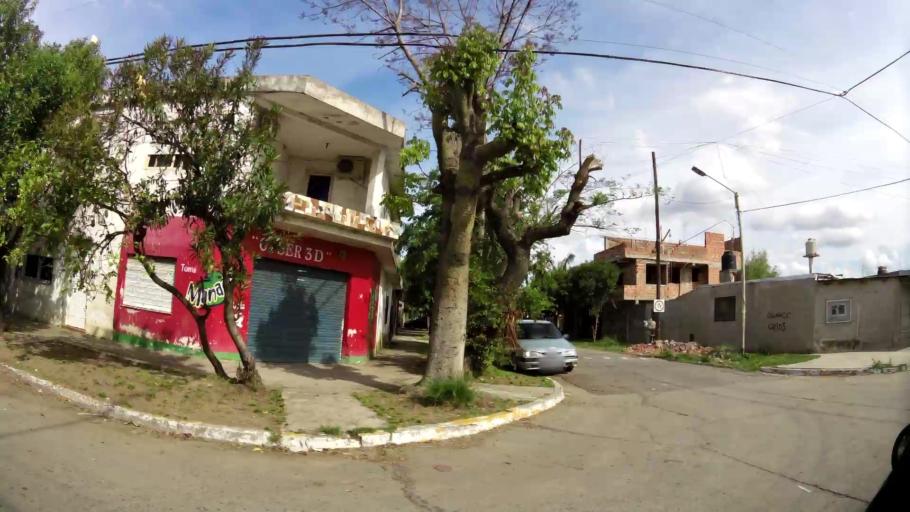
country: AR
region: Buenos Aires
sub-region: Partido de Quilmes
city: Quilmes
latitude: -34.7686
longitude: -58.2482
